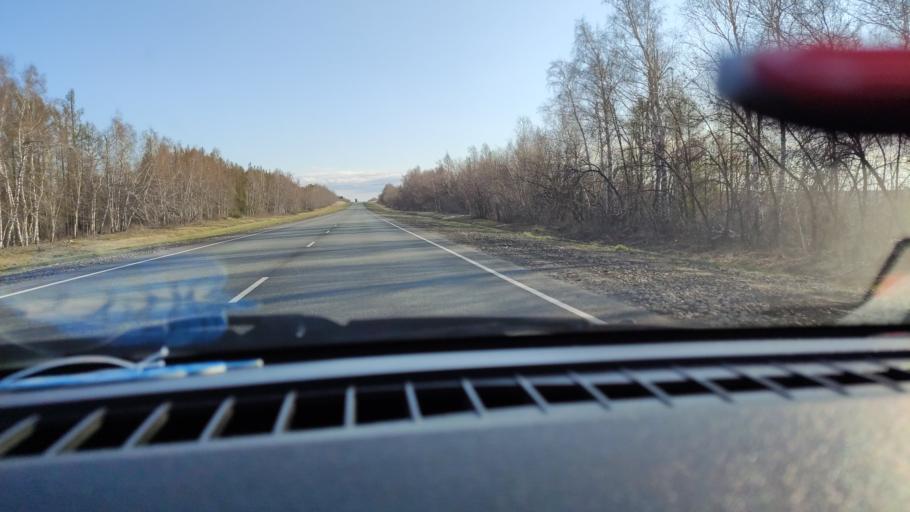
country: RU
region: Saratov
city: Khvalynsk
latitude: 52.5817
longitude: 48.1178
